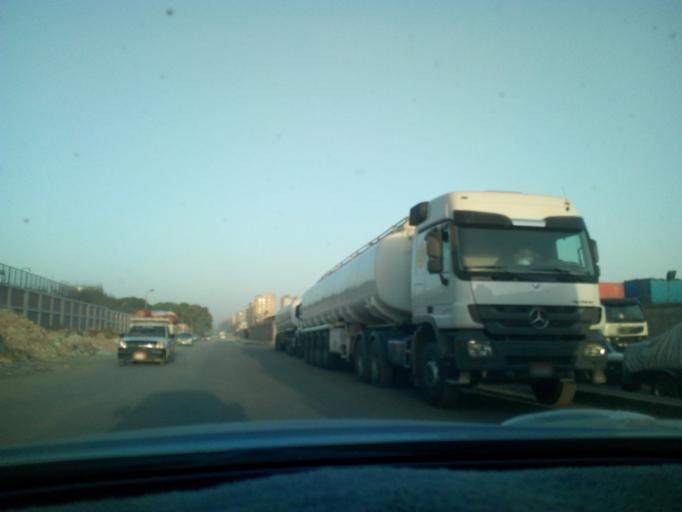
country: EG
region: Muhafazat al Qalyubiyah
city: Al Khankah
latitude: 30.1247
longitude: 31.3587
